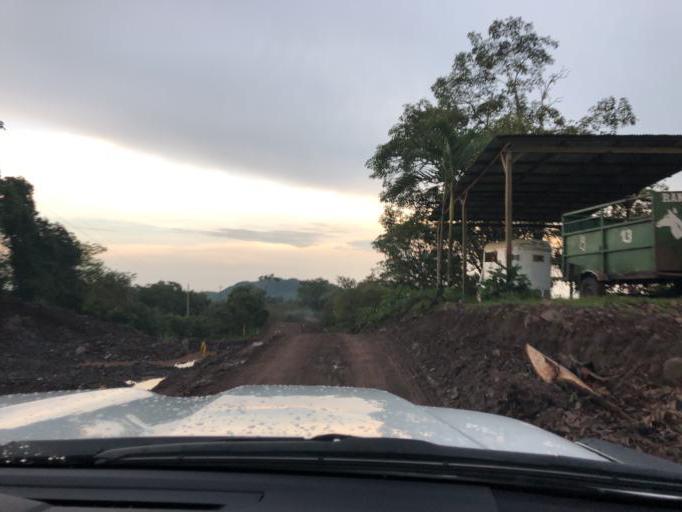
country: NI
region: Chontales
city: La Libertad
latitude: 12.1988
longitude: -85.1775
